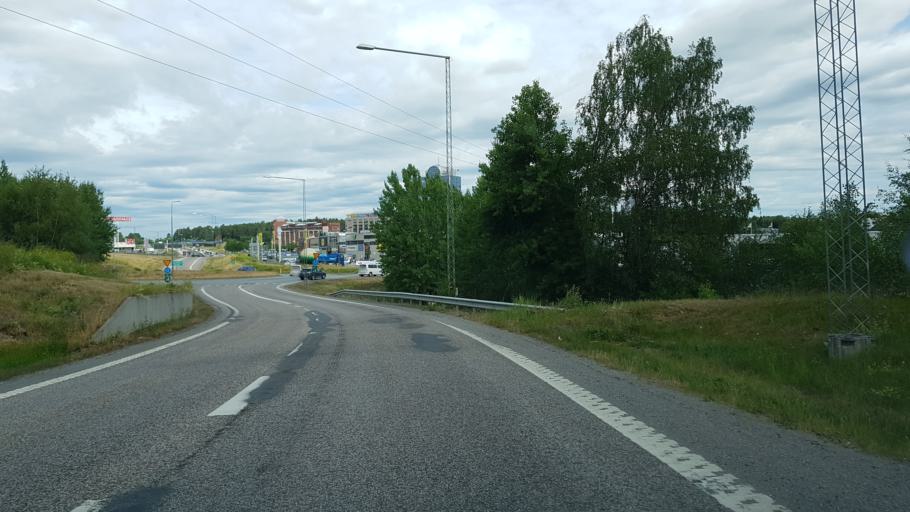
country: SE
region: Stockholm
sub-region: Upplands Vasby Kommun
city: Upplands Vaesby
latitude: 59.4946
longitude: 17.9234
